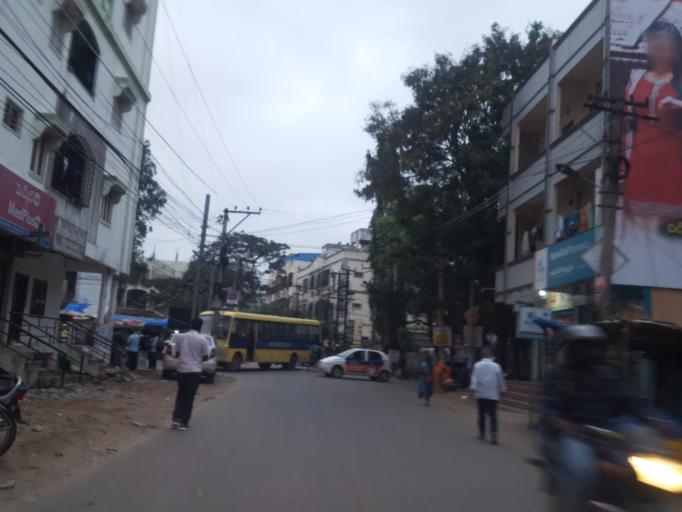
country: IN
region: Telangana
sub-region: Medak
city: Serilingampalle
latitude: 17.4924
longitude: 78.3317
